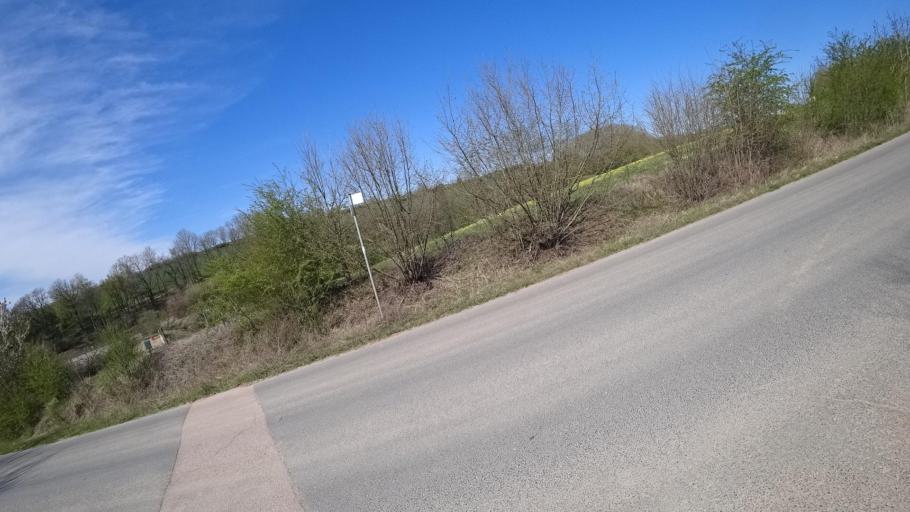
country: DE
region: Rheinland-Pfalz
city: Menningen
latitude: 49.8492
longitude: 6.4940
